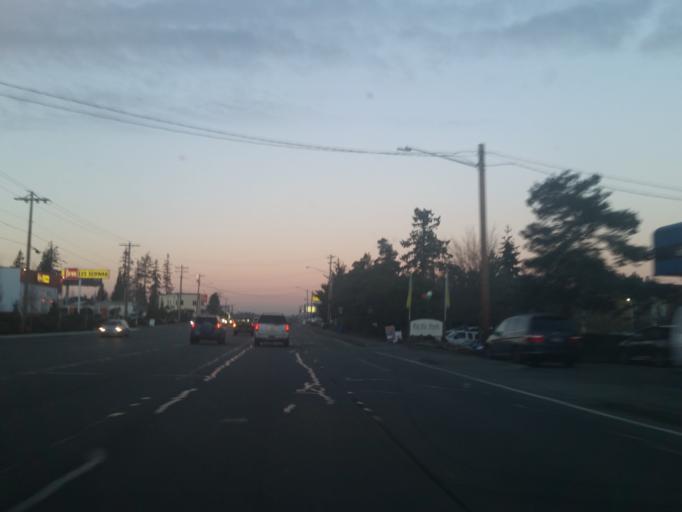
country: US
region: Washington
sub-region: Snohomish County
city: Esperance
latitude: 47.7879
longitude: -122.3402
